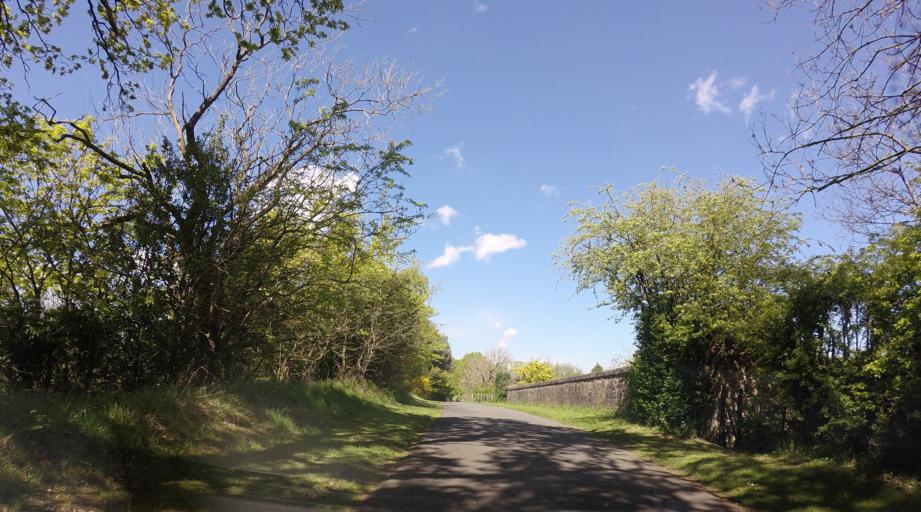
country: GB
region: Scotland
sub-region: Falkirk
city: Polmont
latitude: 55.9731
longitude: -3.6730
